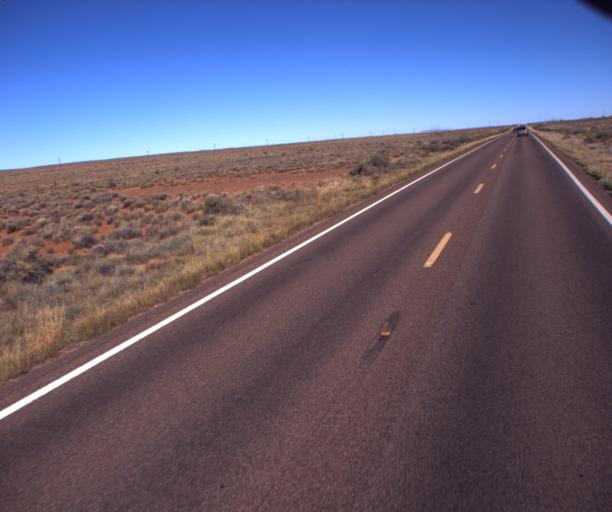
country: US
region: Arizona
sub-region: Navajo County
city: Holbrook
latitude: 34.7833
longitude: -110.1308
